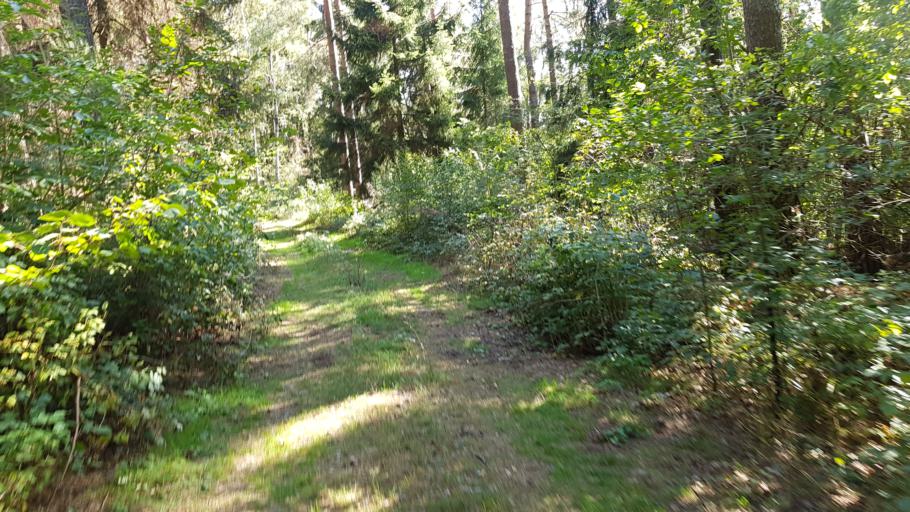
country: DE
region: Saxony
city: Grossnaundorf
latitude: 51.2173
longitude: 13.9539
